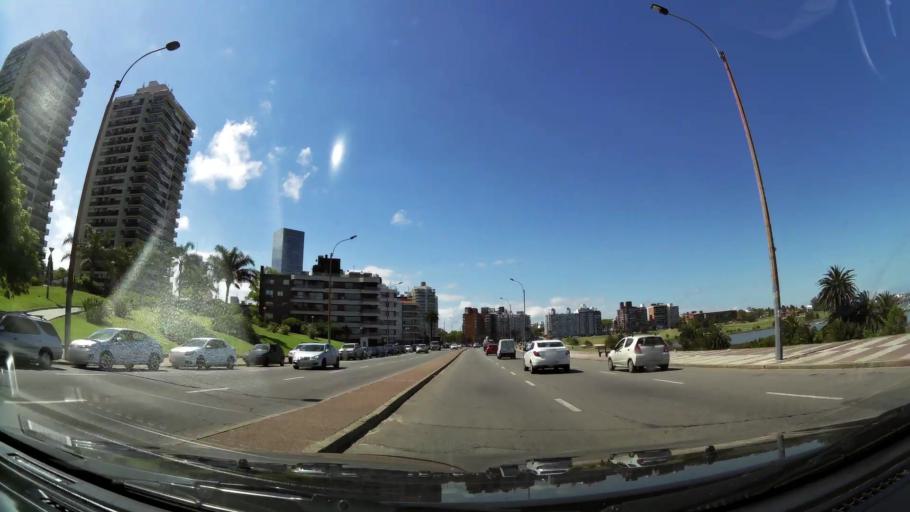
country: UY
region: Montevideo
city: Montevideo
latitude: -34.9088
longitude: -56.1336
